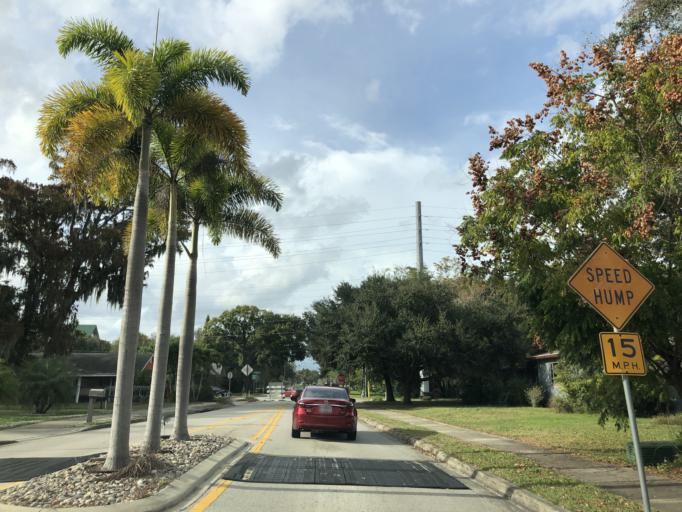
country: US
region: Florida
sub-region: Osceola County
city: Kissimmee
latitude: 28.2934
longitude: -81.4012
